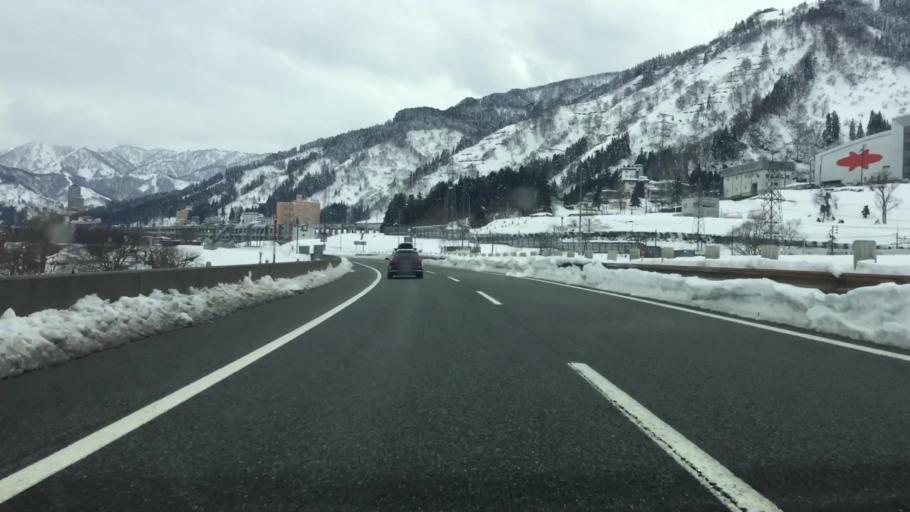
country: JP
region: Niigata
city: Shiozawa
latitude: 36.9531
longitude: 138.8023
